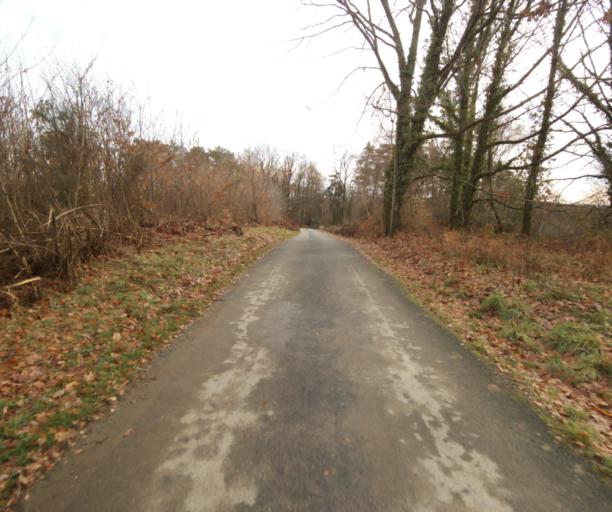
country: FR
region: Limousin
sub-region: Departement de la Correze
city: Chameyrat
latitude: 45.2541
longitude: 1.6853
